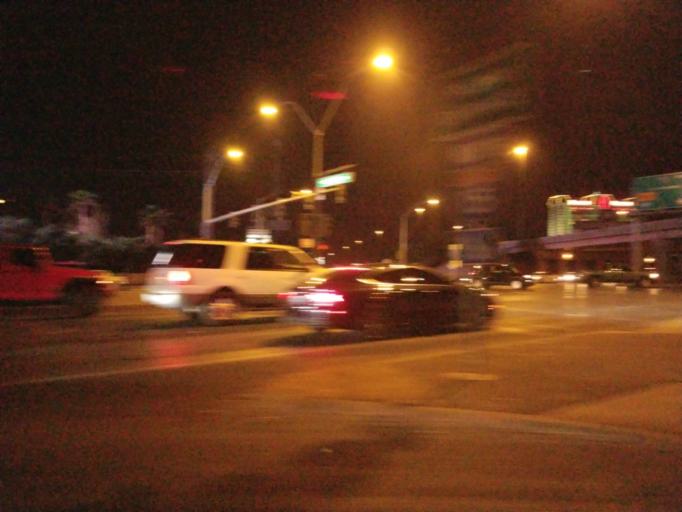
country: US
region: Nevada
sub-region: Clark County
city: Las Vegas
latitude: 36.1444
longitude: -115.1700
